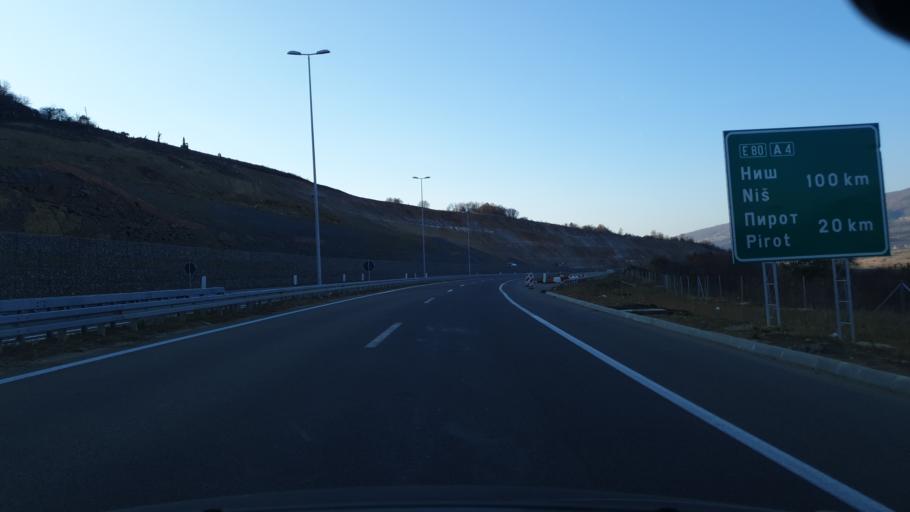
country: RS
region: Central Serbia
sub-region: Pirotski Okrug
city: Dimitrovgrad
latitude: 43.0029
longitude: 22.8082
